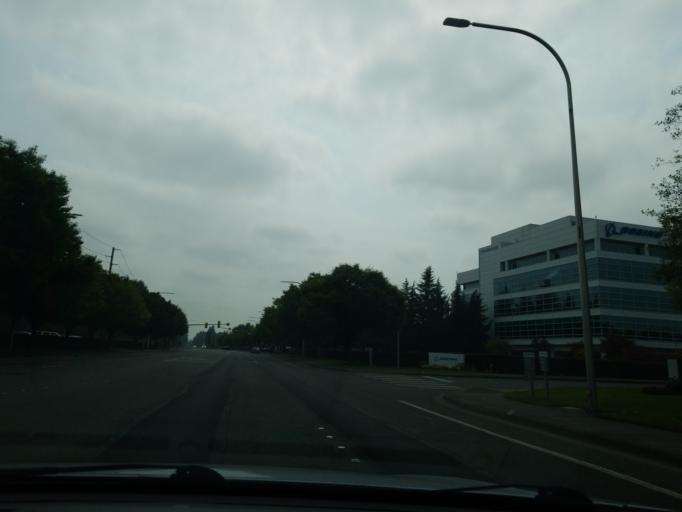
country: US
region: Washington
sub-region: King County
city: Renton
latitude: 47.4630
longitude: -122.2328
